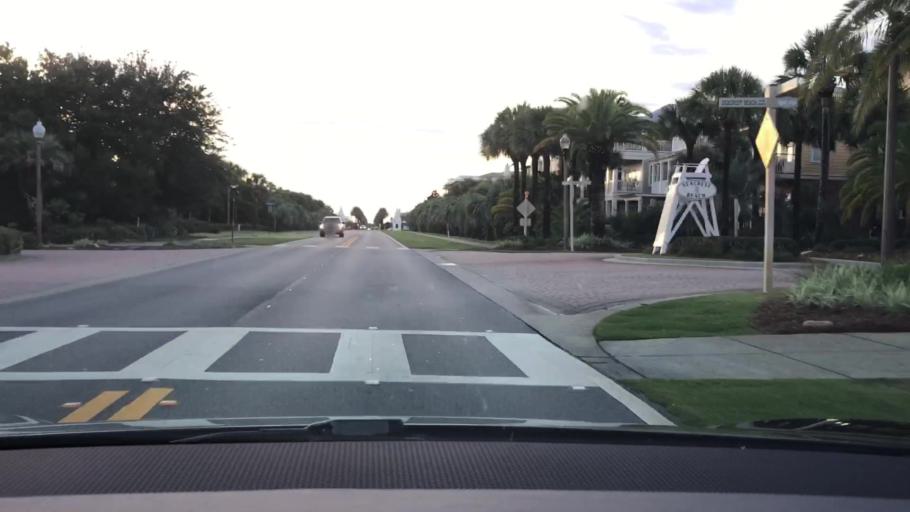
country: US
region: Florida
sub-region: Bay County
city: Laguna Beach
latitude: 30.2821
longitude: -86.0217
